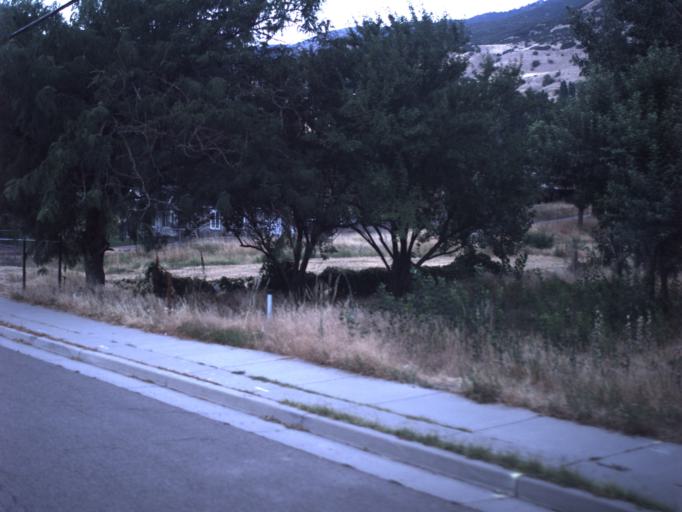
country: US
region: Utah
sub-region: Davis County
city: Centerville
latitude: 40.9400
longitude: -111.8798
